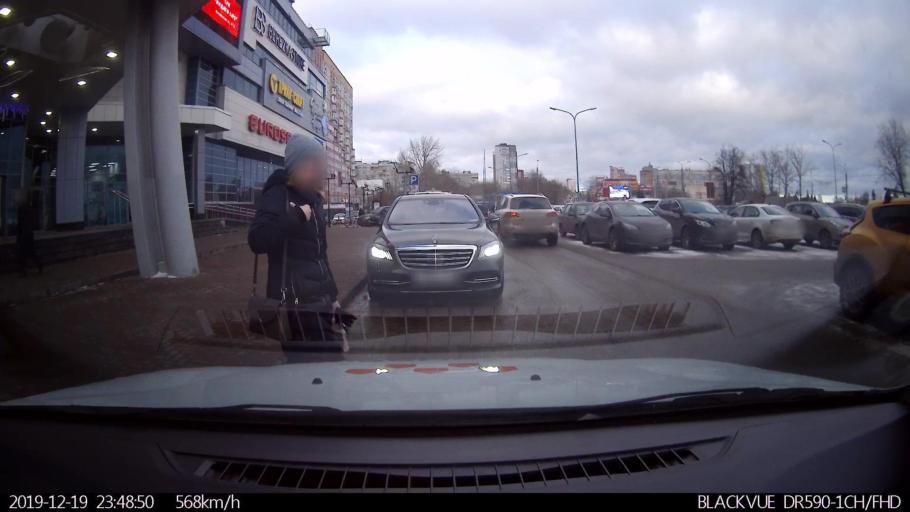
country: RU
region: Jaroslavl
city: Borok
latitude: 58.3099
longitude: 38.4498
